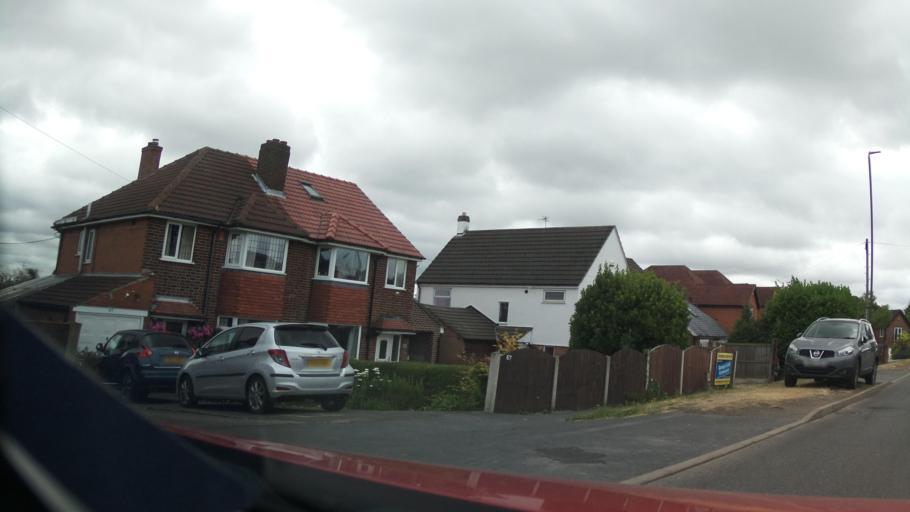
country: GB
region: England
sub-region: Derbyshire
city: Ripley
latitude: 52.9947
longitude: -1.3942
